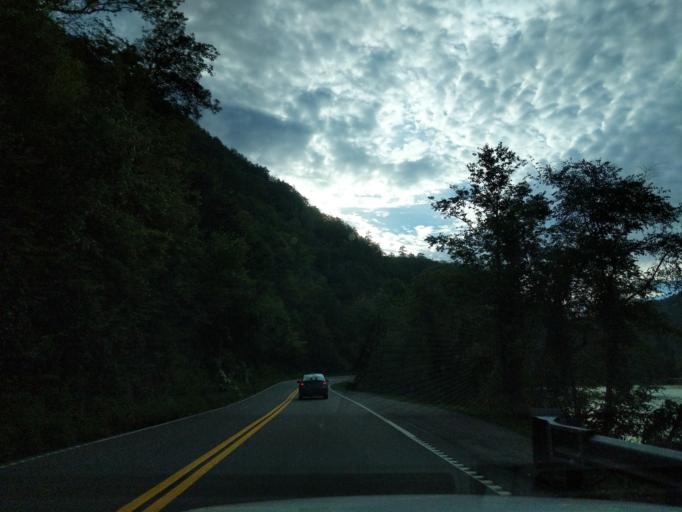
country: US
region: Tennessee
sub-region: Polk County
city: Benton
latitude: 35.0994
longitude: -84.5541
